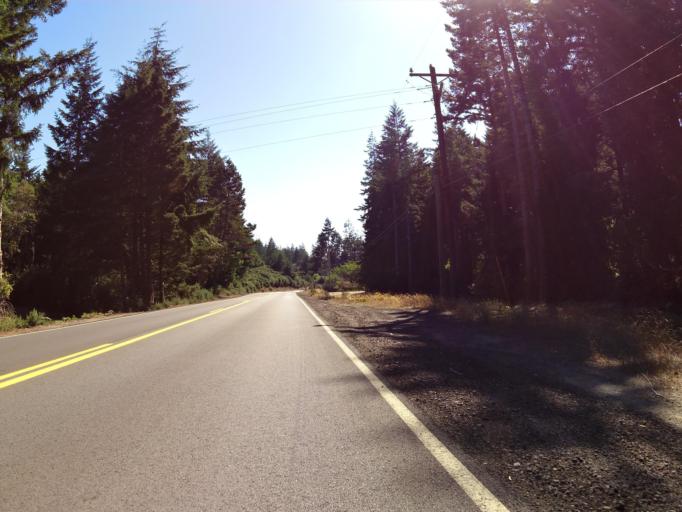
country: US
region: Oregon
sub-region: Coos County
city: Bandon
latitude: 43.1968
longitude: -124.3661
